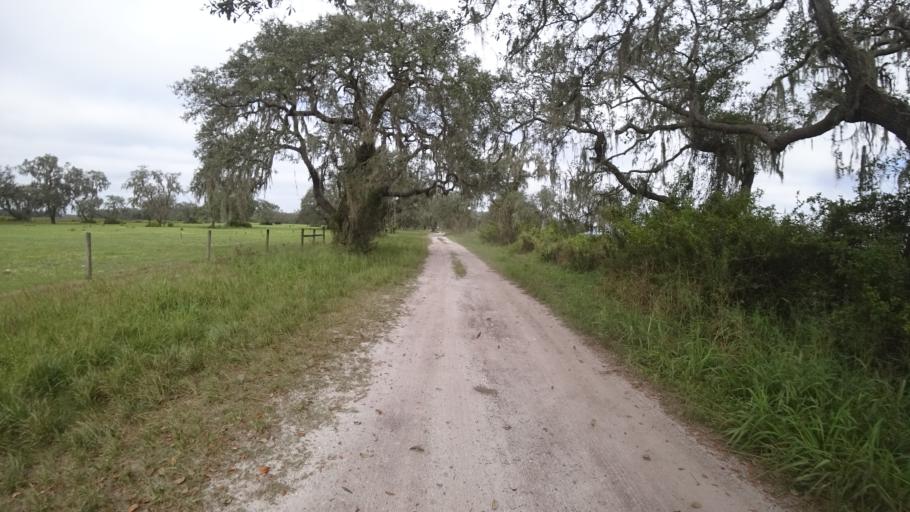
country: US
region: Florida
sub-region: Sarasota County
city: Warm Mineral Springs
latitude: 27.3222
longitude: -82.1379
